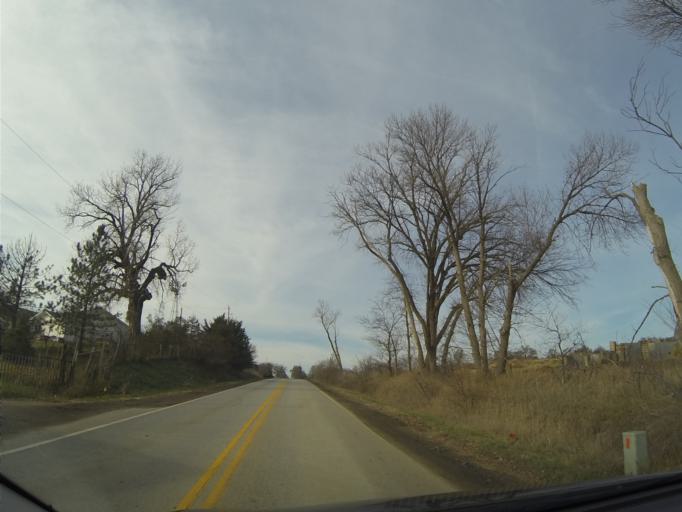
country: US
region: Nebraska
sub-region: Douglas County
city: Elkhorn
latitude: 41.2775
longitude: -96.2082
